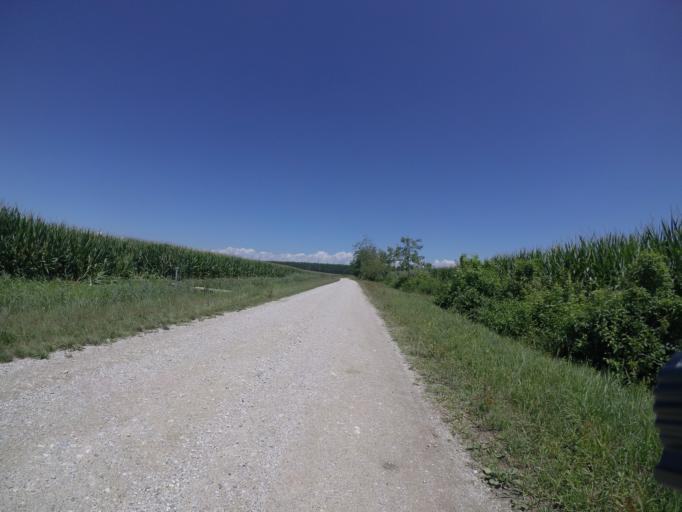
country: IT
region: Friuli Venezia Giulia
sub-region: Provincia di Udine
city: Talmassons
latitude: 45.8944
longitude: 13.0969
